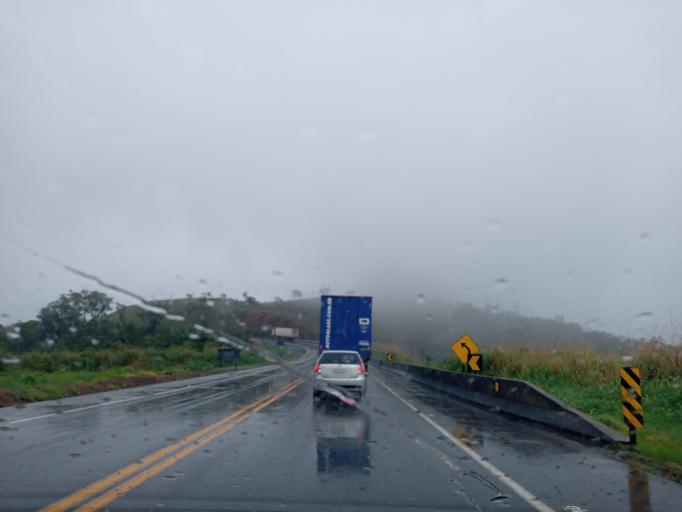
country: BR
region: Minas Gerais
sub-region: Luz
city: Luz
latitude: -19.7163
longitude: -45.8826
